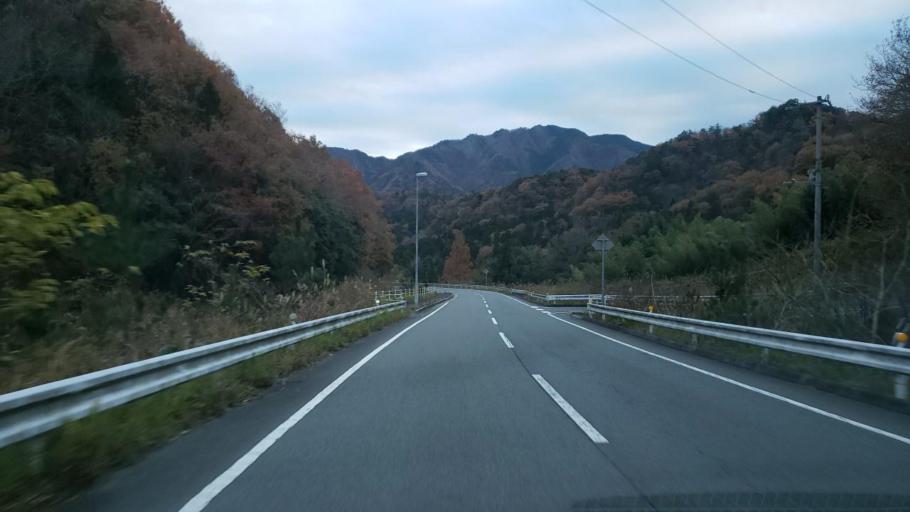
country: JP
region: Kagawa
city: Shido
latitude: 34.1908
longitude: 134.2194
